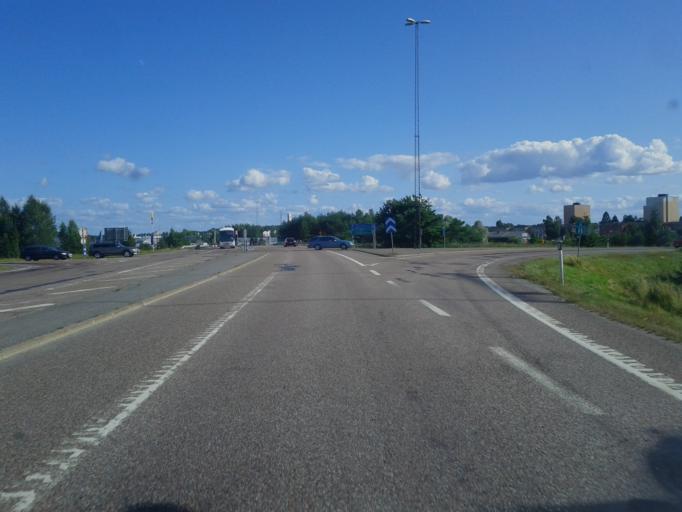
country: SE
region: Uppsala
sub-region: Enkopings Kommun
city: Enkoping
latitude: 59.6564
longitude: 17.0791
